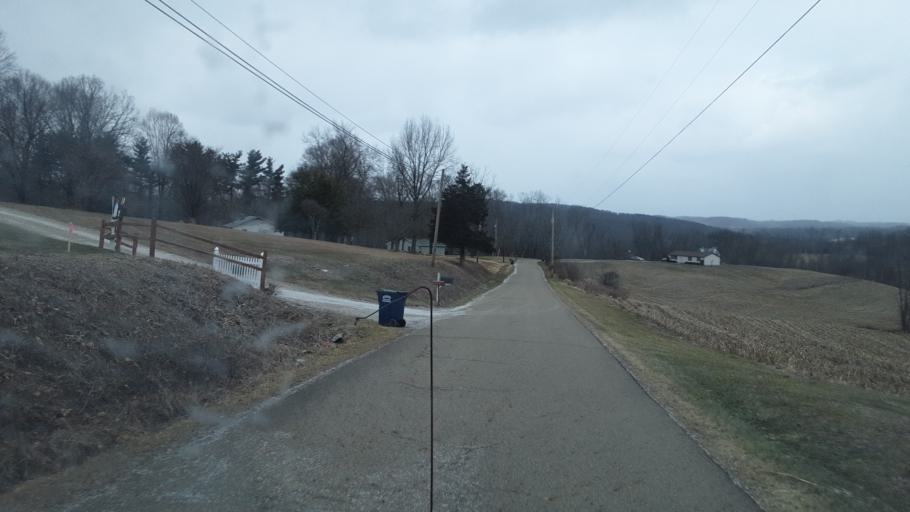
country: US
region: Ohio
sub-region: Perry County
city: Thornport
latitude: 39.9491
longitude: -82.3508
